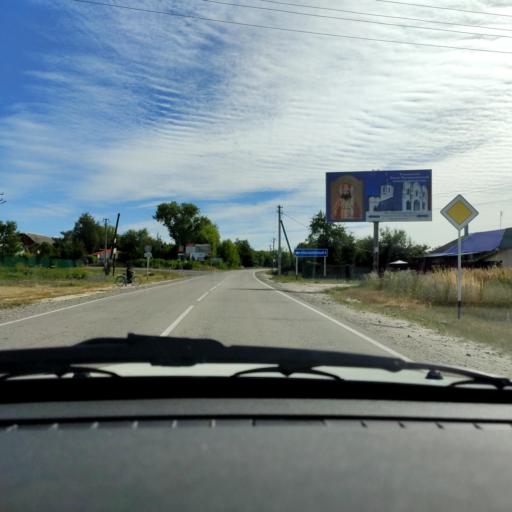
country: RU
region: Voronezj
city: Uglyanets
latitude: 51.8590
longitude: 39.6723
